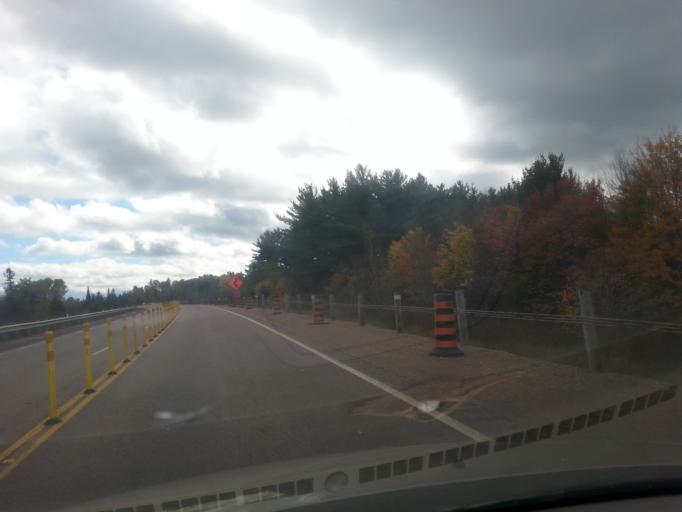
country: CA
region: Ontario
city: Pembroke
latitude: 45.8045
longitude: -77.2004
